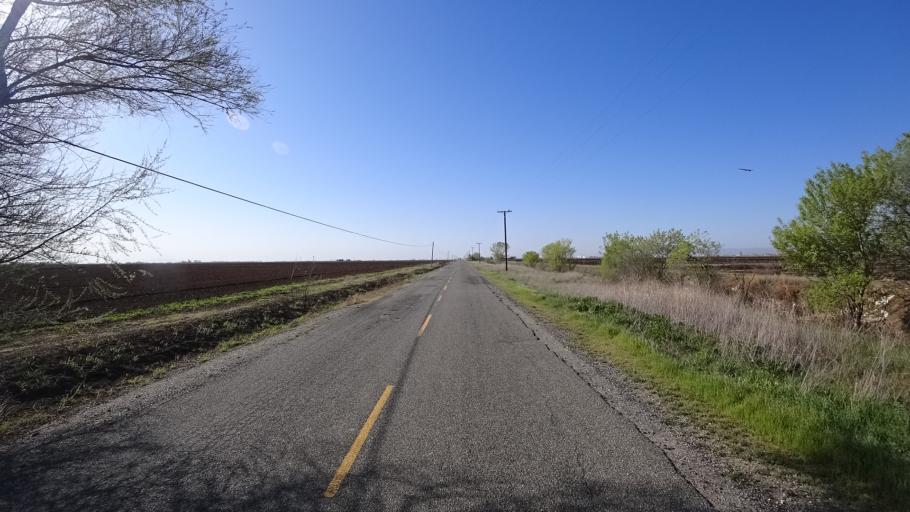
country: US
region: California
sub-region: Glenn County
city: Willows
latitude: 39.5070
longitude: -122.1745
